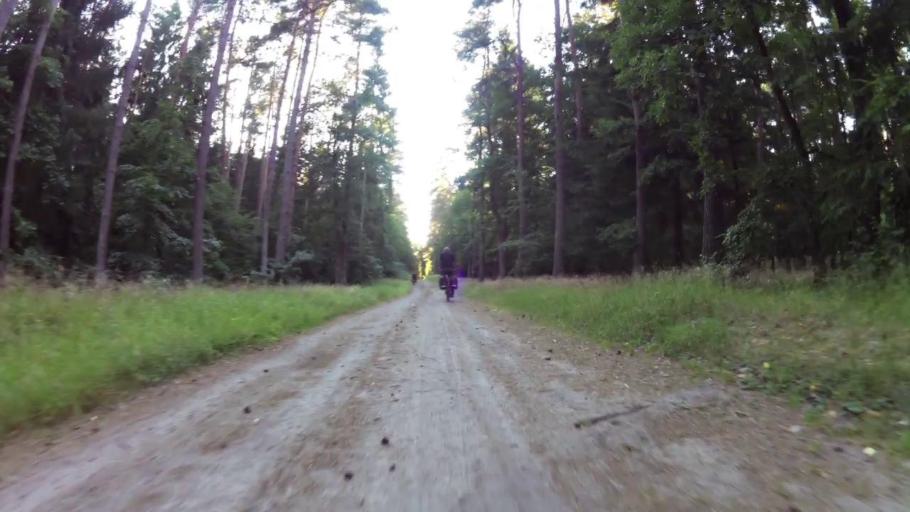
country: PL
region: West Pomeranian Voivodeship
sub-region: Powiat lobeski
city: Lobez
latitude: 53.7448
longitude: 15.6472
